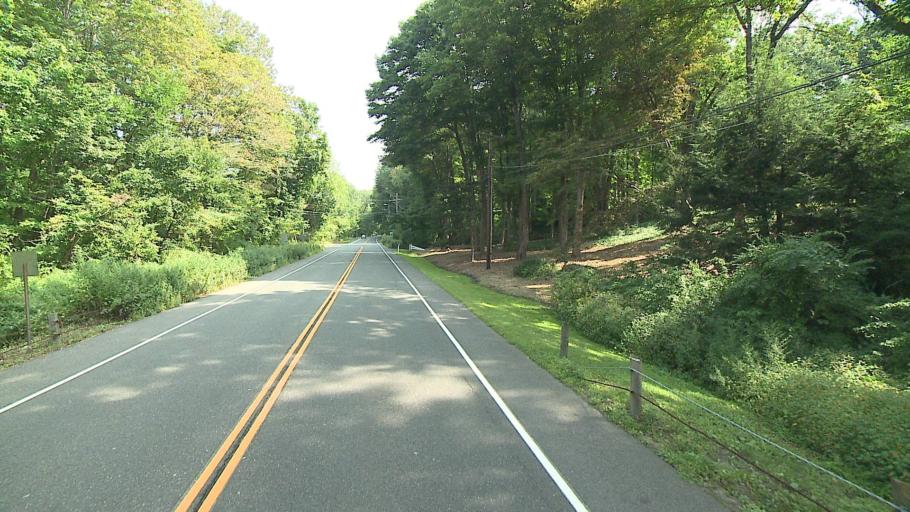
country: US
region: Connecticut
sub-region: Fairfield County
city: Ridgefield
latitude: 41.2662
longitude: -73.5193
